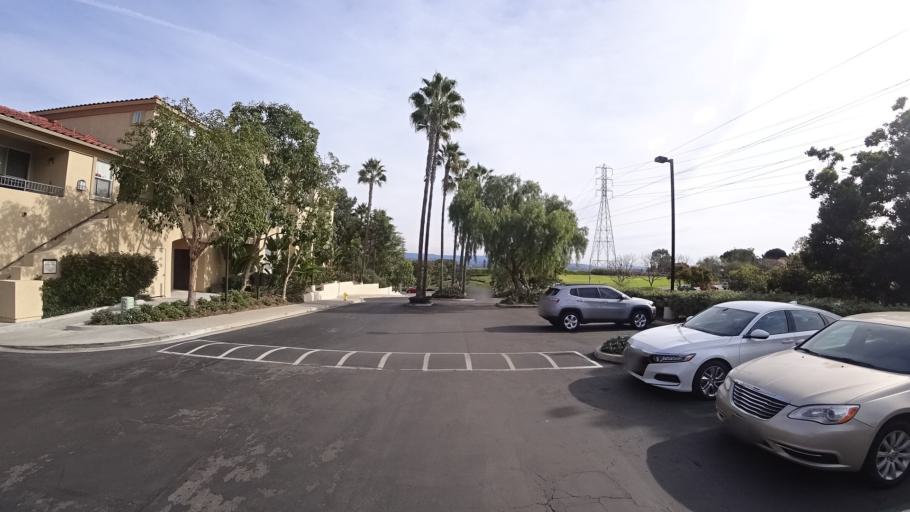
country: US
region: California
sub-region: Orange County
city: Laguna Woods
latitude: 33.5942
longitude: -117.7330
